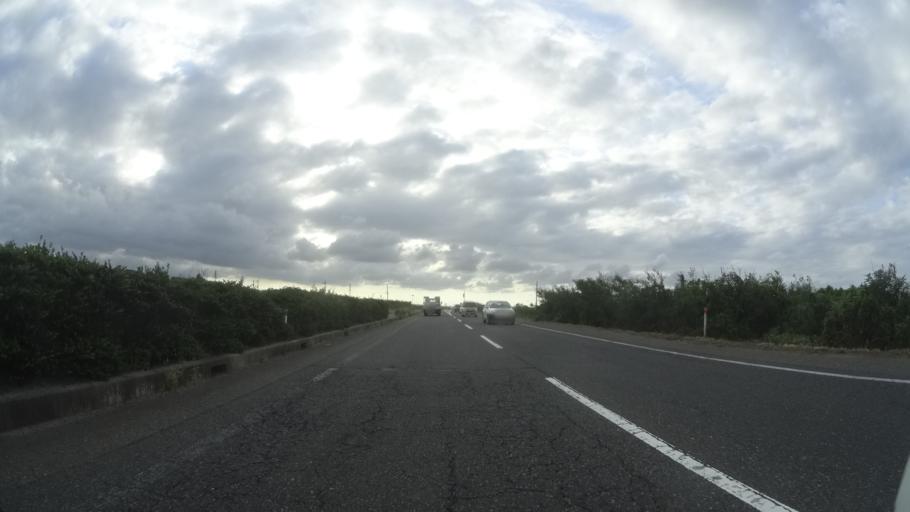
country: JP
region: Tottori
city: Kurayoshi
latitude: 35.5002
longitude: 133.7458
